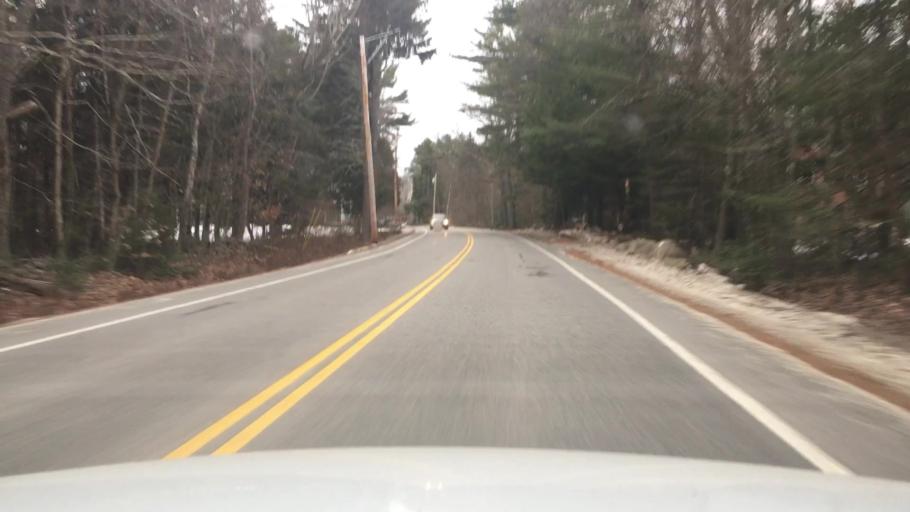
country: US
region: Maine
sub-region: Cumberland County
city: Freeport
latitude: 43.8638
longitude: -70.0709
